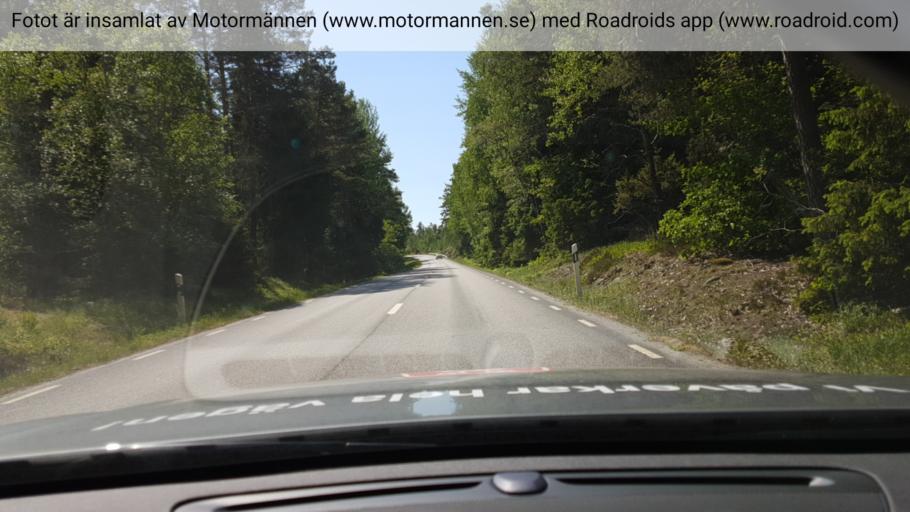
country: SE
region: Stockholm
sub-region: Norrtalje Kommun
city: Rimbo
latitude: 59.6709
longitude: 18.3535
